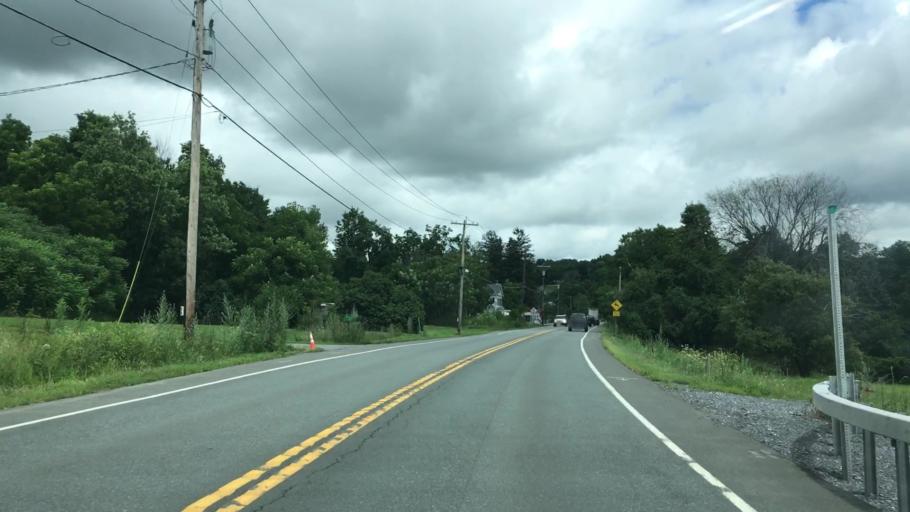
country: US
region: New York
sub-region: Rensselaer County
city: Hoosick Falls
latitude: 42.8763
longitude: -73.3037
